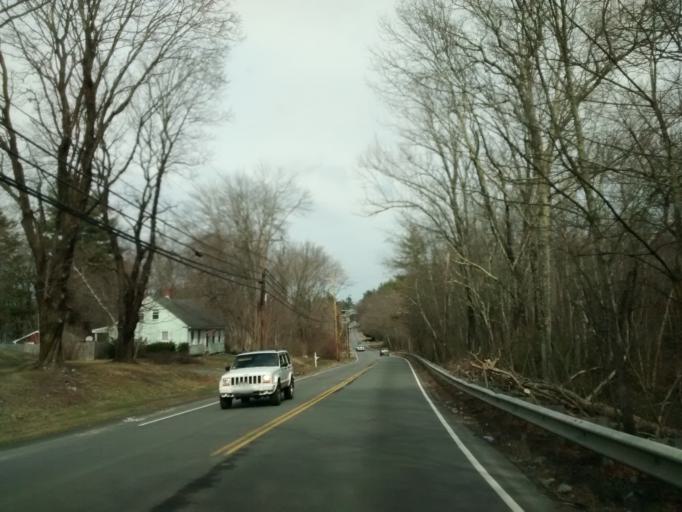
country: US
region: Massachusetts
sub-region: Worcester County
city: Douglas
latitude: 42.0635
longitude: -71.7268
